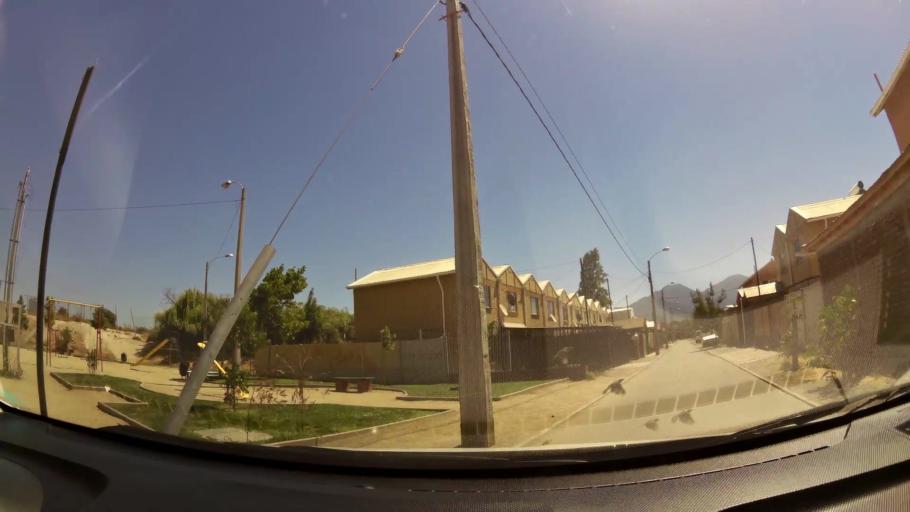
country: CL
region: O'Higgins
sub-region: Provincia de Cachapoal
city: Rancagua
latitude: -34.1721
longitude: -70.7831
